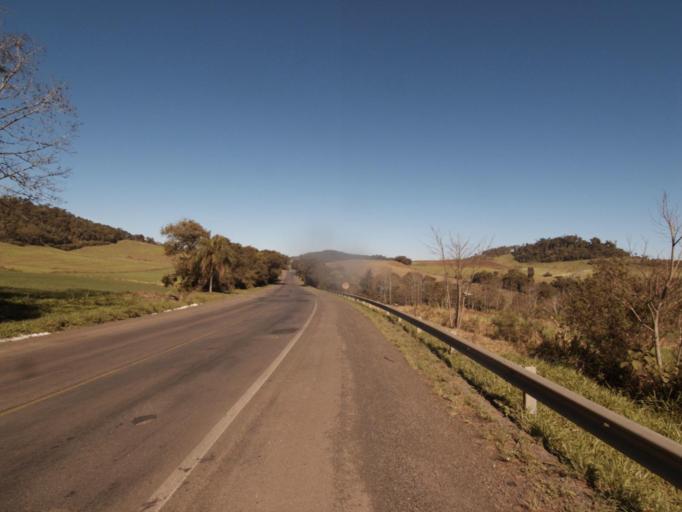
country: BR
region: Rio Grande do Sul
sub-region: Frederico Westphalen
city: Frederico Westphalen
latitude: -26.8064
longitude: -53.3634
